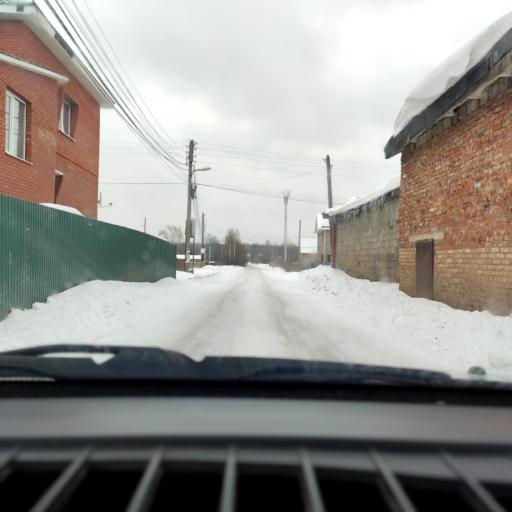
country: RU
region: Perm
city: Krasnokamsk
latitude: 58.0956
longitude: 55.8021
